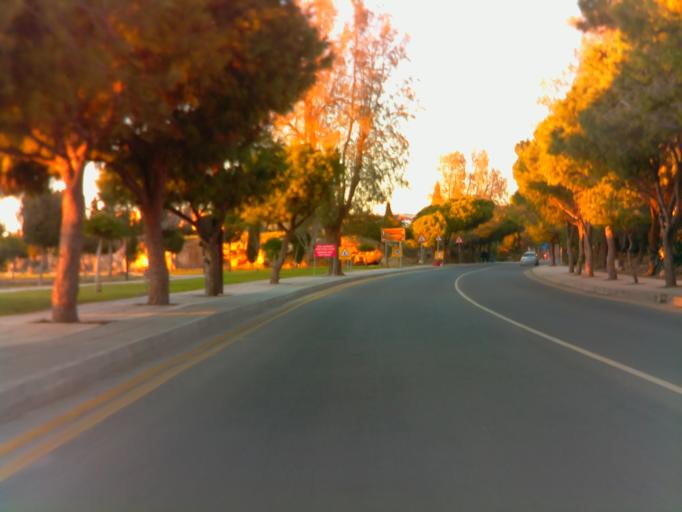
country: CY
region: Pafos
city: Paphos
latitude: 34.7618
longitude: 32.4123
